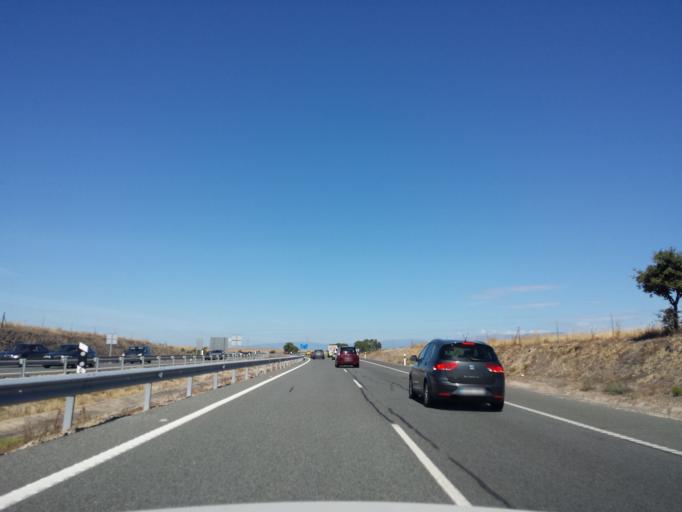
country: ES
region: Castille-La Mancha
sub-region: Province of Toledo
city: Oropesa
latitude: 39.9257
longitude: -5.1899
